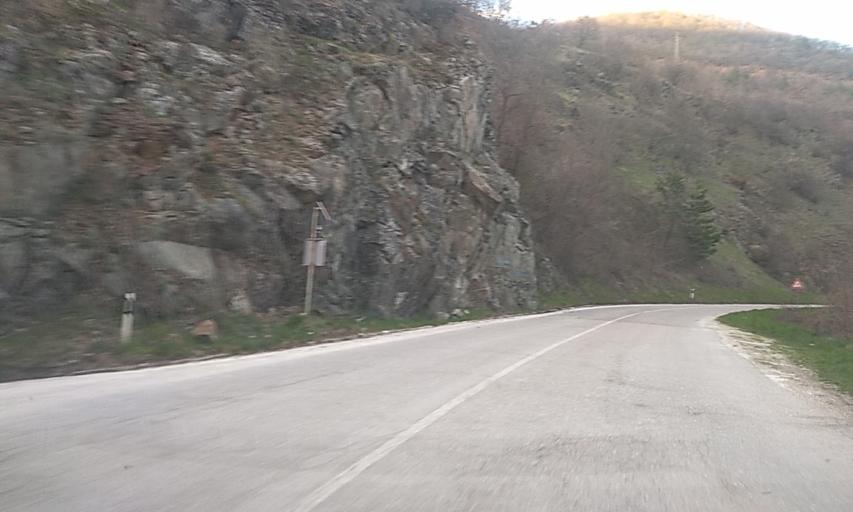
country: RS
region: Central Serbia
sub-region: Pcinjski Okrug
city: Bosilegrad
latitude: 42.4983
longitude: 22.4600
